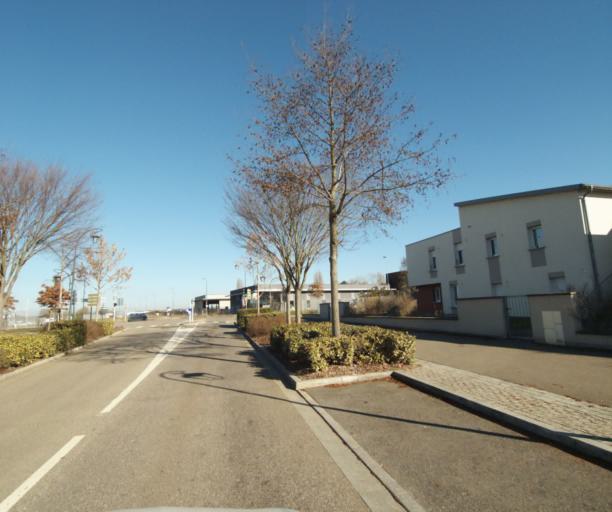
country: FR
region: Lorraine
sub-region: Departement de Meurthe-et-Moselle
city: Tomblaine
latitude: 48.6892
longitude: 6.2147
